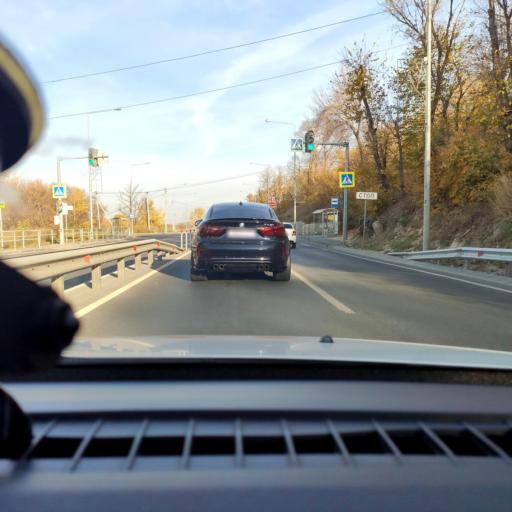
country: RU
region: Samara
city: Volzhskiy
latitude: 53.3934
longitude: 50.1553
